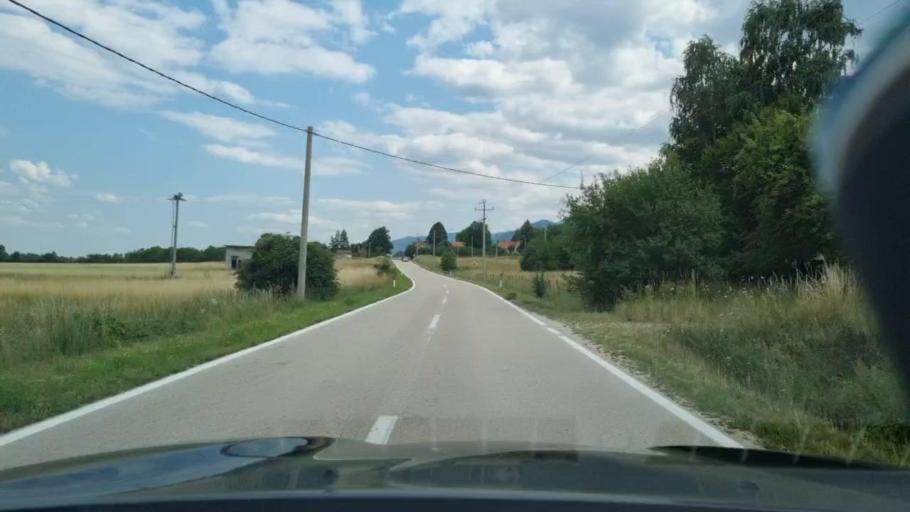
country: BA
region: Federation of Bosnia and Herzegovina
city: Glamoc
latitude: 44.0455
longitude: 16.5892
